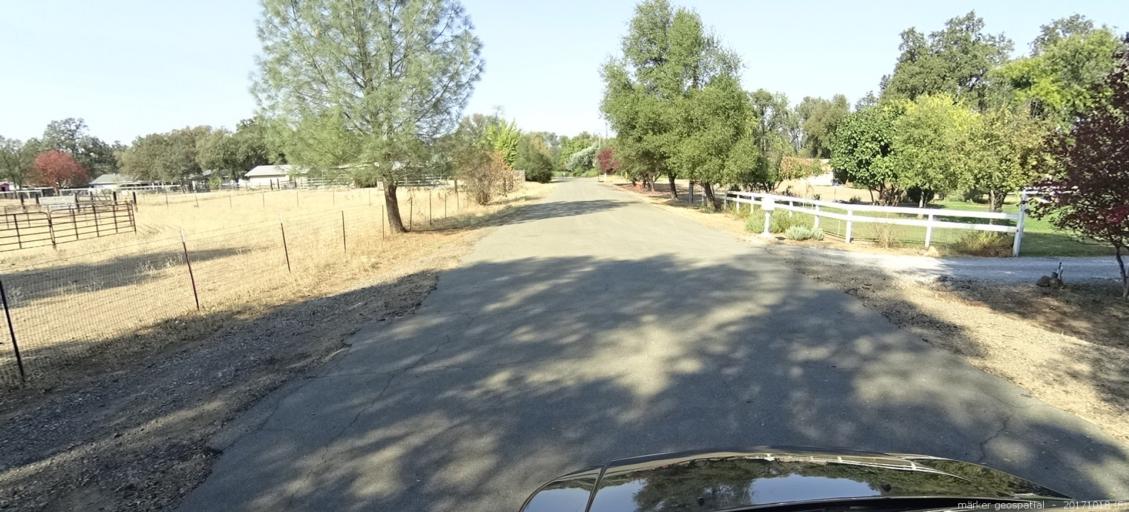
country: US
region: California
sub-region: Shasta County
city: Palo Cedro
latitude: 40.5711
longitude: -122.2285
